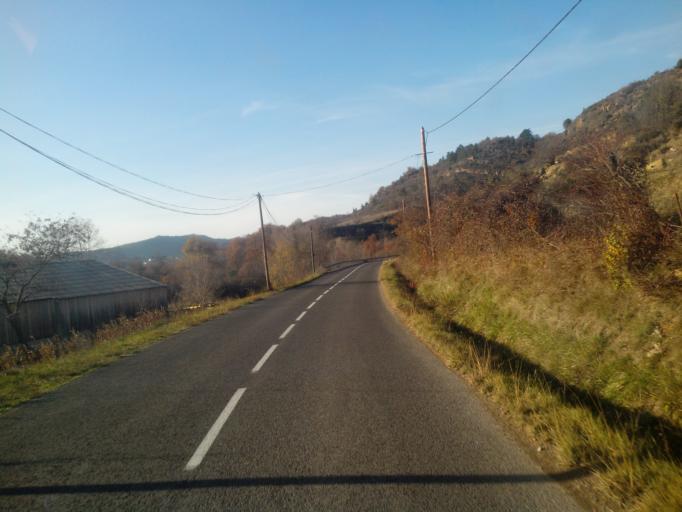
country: FR
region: Languedoc-Roussillon
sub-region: Departement de l'Aude
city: Couiza
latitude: 42.9386
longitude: 2.2752
